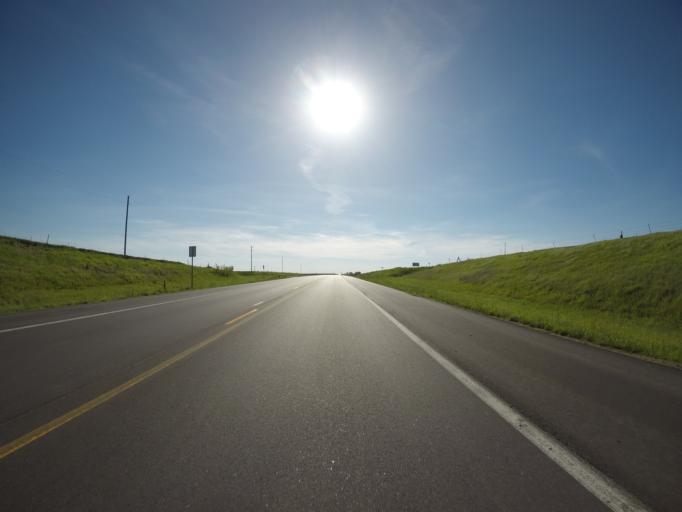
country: US
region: Kansas
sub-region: Clay County
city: Clay Center
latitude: 39.3796
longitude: -96.9789
